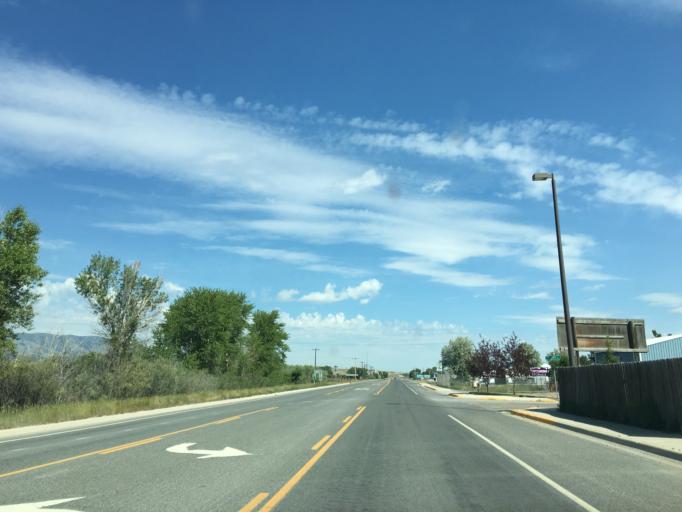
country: US
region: Montana
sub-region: Broadwater County
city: Townsend
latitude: 46.3258
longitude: -111.5258
